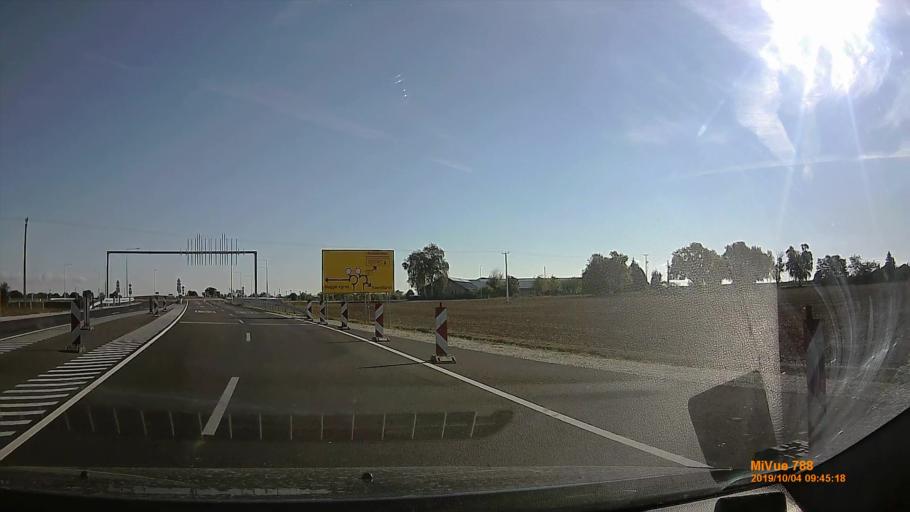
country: HU
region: Somogy
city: Kaposvar
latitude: 46.4240
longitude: 17.7726
